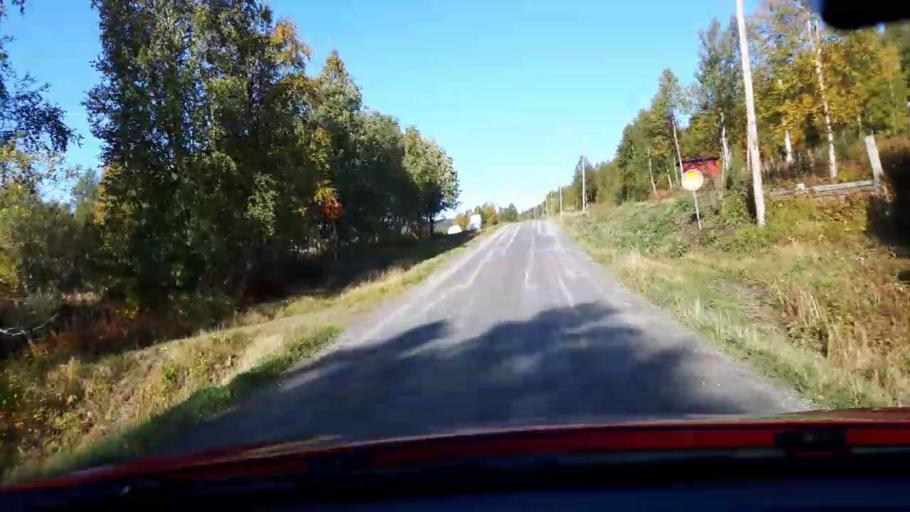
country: NO
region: Nord-Trondelag
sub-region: Lierne
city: Sandvika
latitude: 64.6041
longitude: 13.7863
